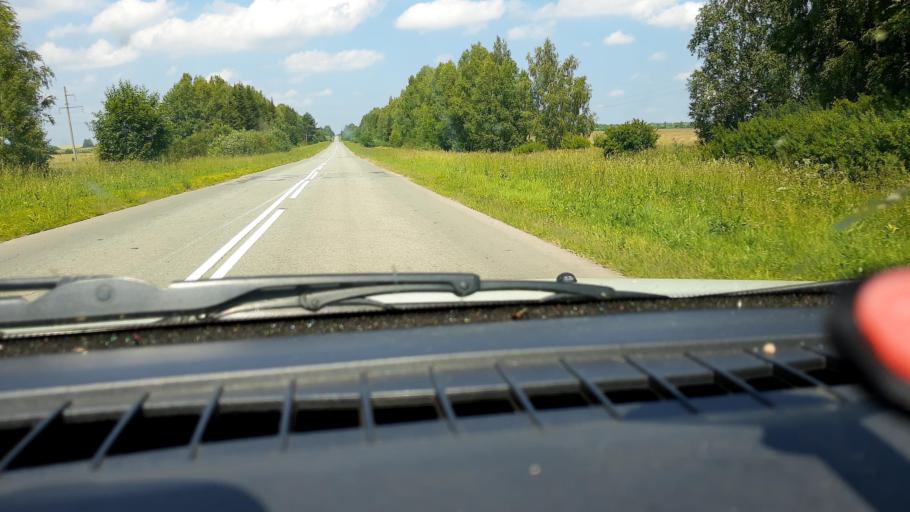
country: RU
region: Nizjnij Novgorod
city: Sharanga
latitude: 57.0855
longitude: 46.5356
